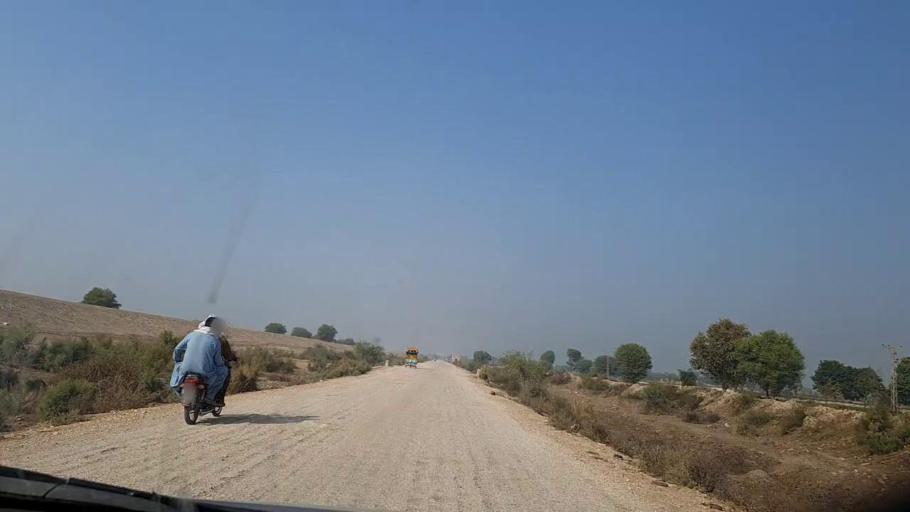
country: PK
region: Sindh
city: Moro
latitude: 26.7210
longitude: 67.9228
